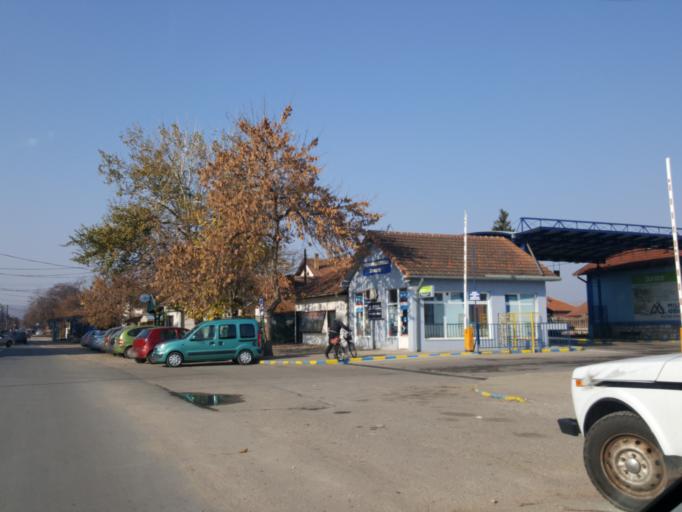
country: RS
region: Central Serbia
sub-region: Borski Okrug
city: Negotin
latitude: 44.2281
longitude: 22.5405
